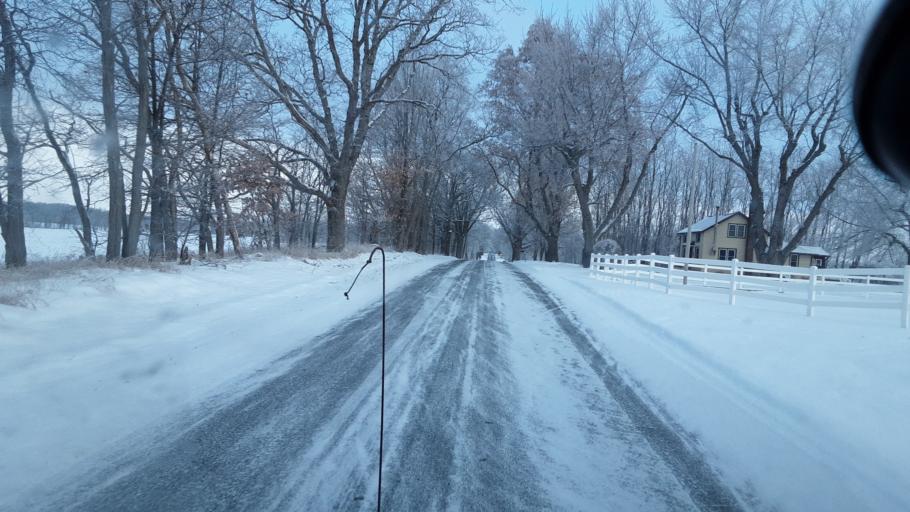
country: US
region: Michigan
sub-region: Ingham County
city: Leslie
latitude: 42.4309
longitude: -84.4970
